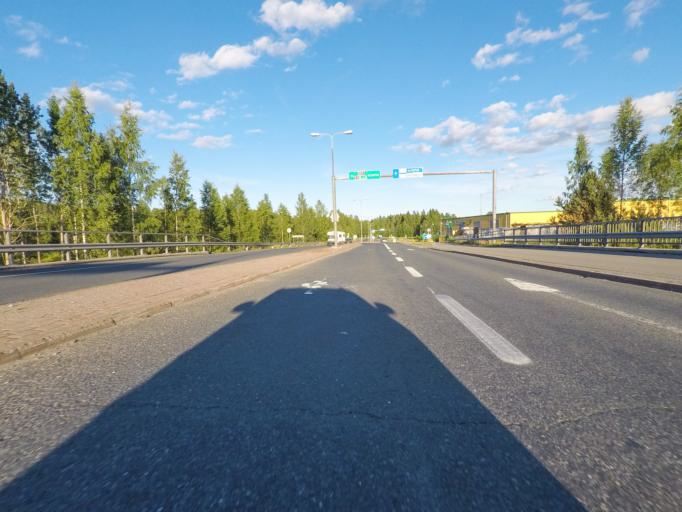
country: FI
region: Northern Savo
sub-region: Kuopio
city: Kuopio
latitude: 62.8411
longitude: 27.6058
